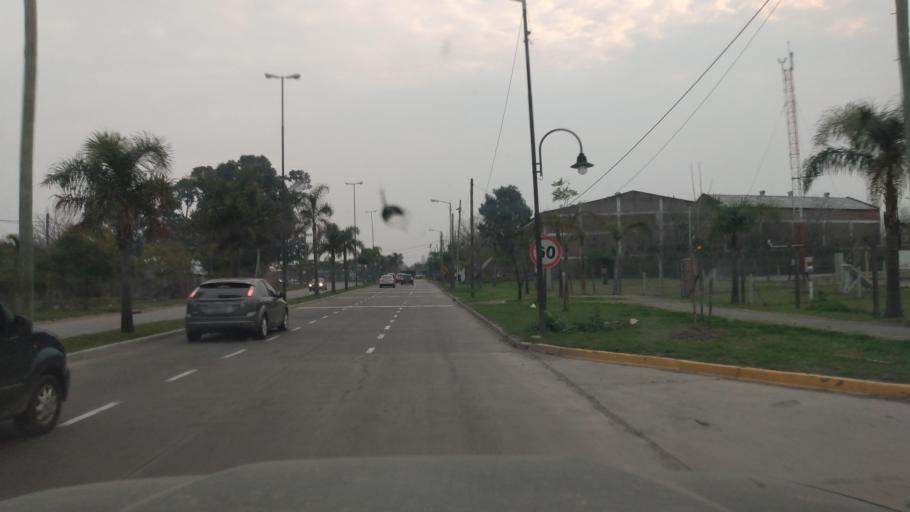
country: AR
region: Buenos Aires
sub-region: Partido de Tigre
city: Tigre
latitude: -34.4603
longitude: -58.5927
